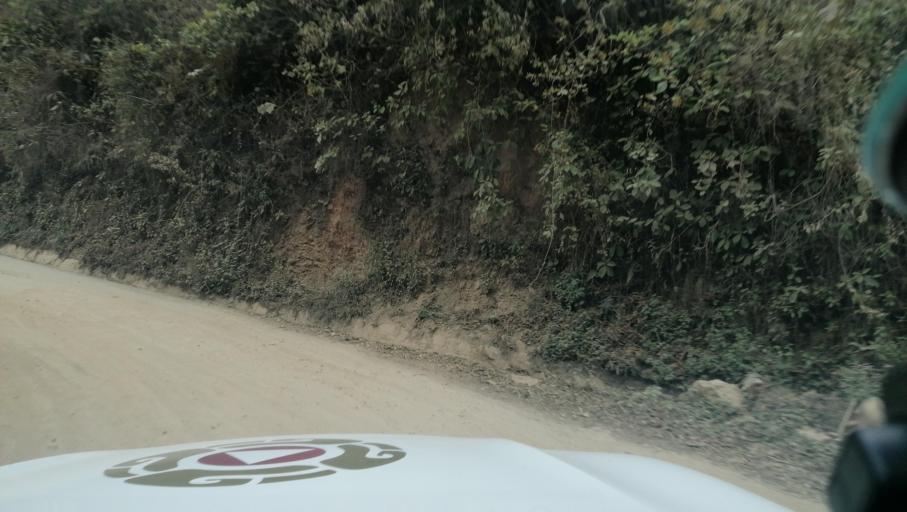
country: GT
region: San Marcos
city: Tacana
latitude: 15.2131
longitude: -92.1984
